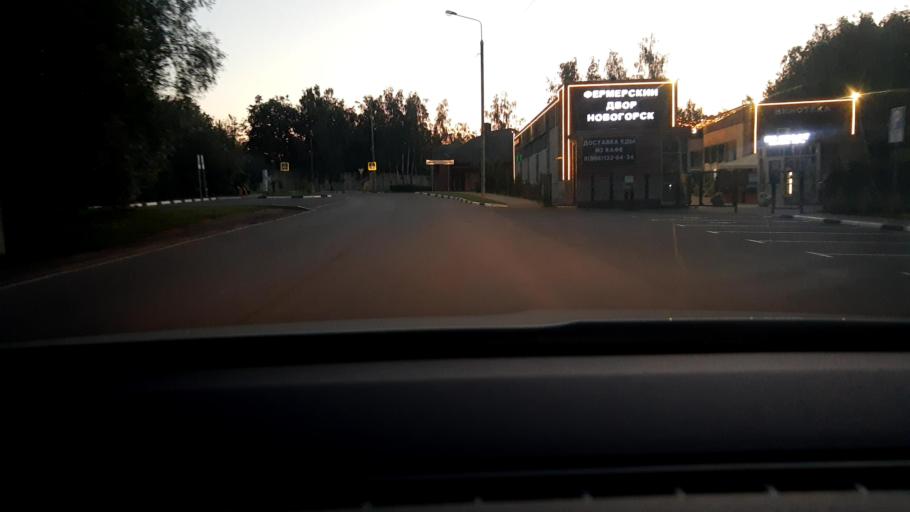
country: RU
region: Moskovskaya
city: Novopodrezkovo
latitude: 55.8882
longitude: 37.3622
